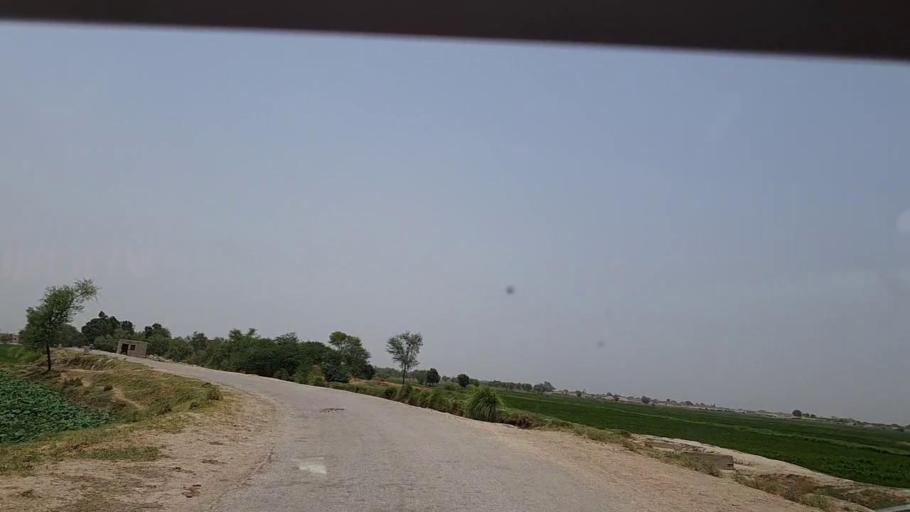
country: PK
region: Sindh
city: Khairpur Nathan Shah
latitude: 27.0142
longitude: 67.6709
